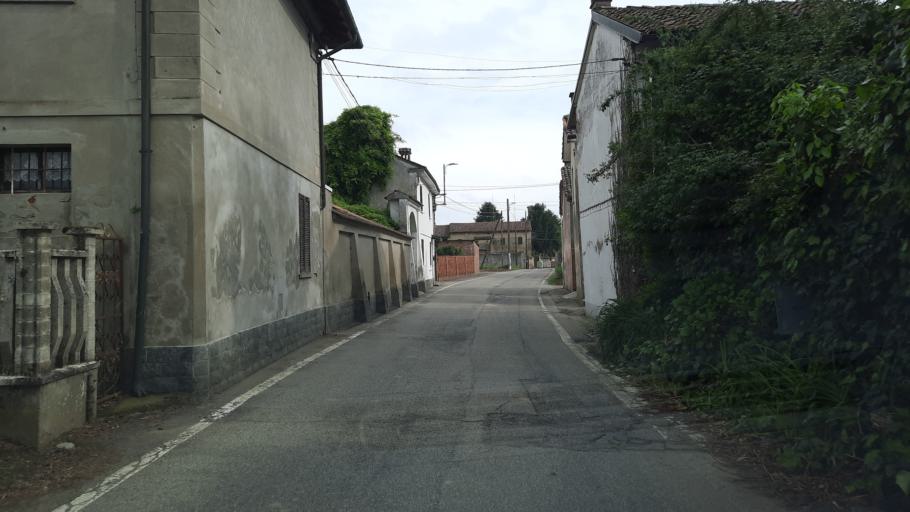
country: IT
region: Lombardy
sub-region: Provincia di Pavia
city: Castelnovetto
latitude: 45.2294
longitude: 8.6024
